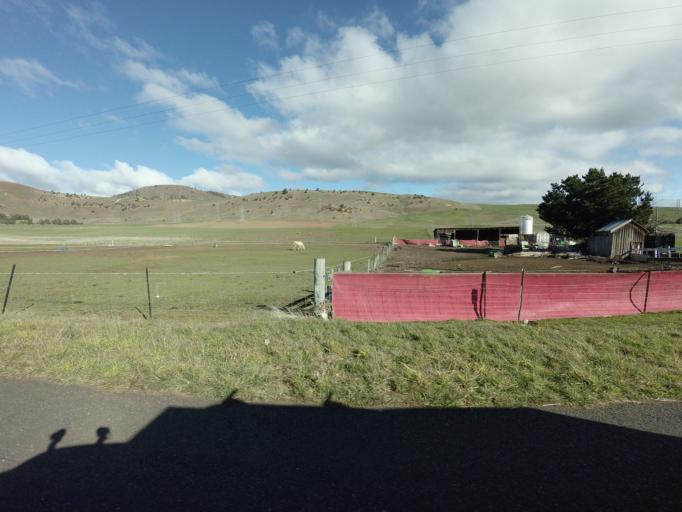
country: AU
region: Tasmania
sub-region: Derwent Valley
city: New Norfolk
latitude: -42.6942
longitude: 146.9680
